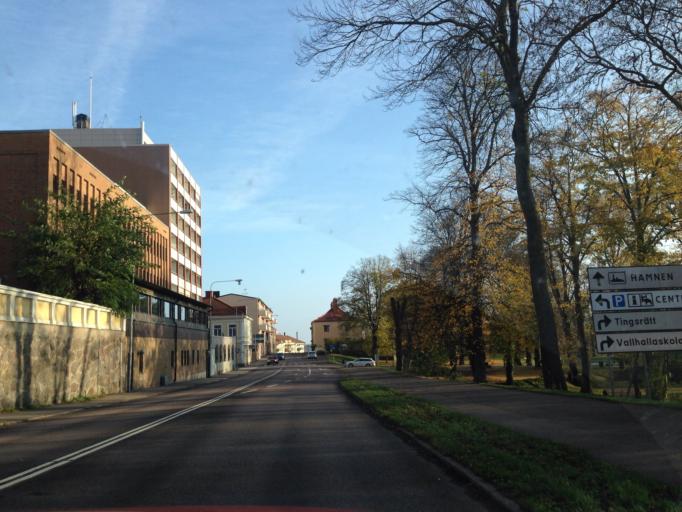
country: SE
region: Kalmar
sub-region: Oskarshamns Kommun
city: Oskarshamn
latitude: 57.2637
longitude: 16.4481
